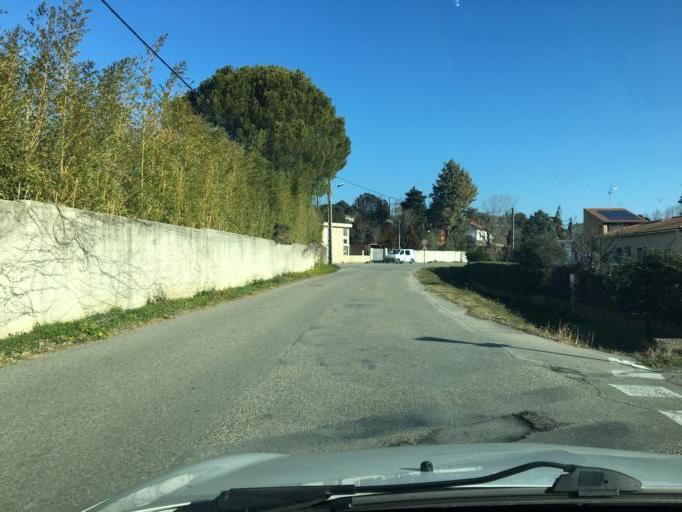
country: FR
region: Languedoc-Roussillon
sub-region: Departement du Gard
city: Les Angles
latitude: 43.9485
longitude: 4.7817
